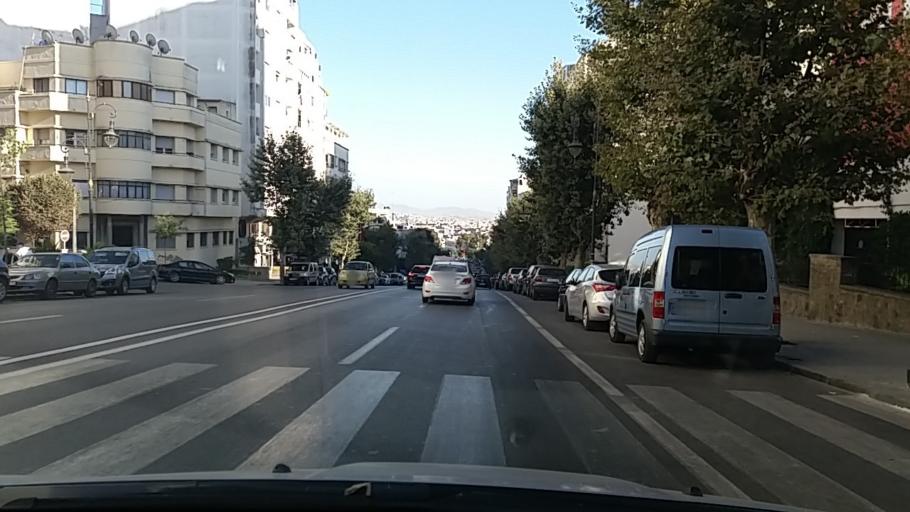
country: MA
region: Tanger-Tetouan
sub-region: Tanger-Assilah
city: Tangier
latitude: 35.7802
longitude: -5.8204
